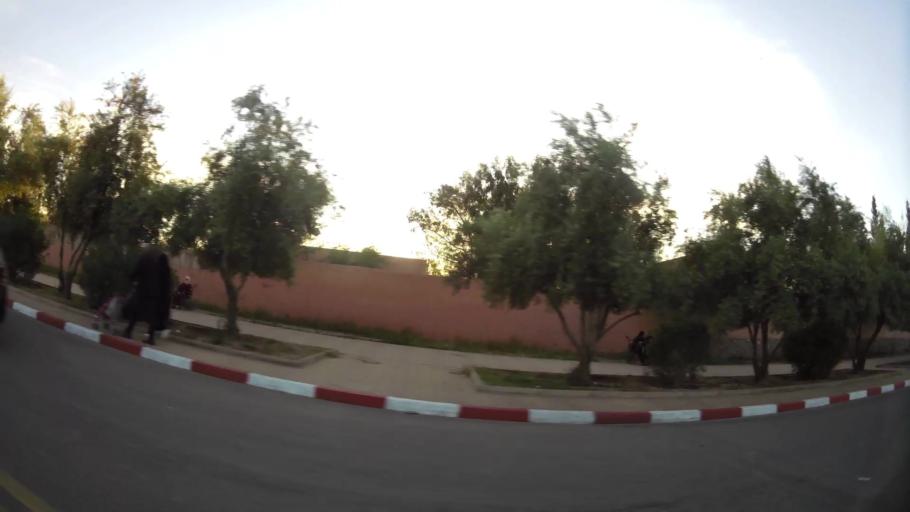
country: MA
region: Marrakech-Tensift-Al Haouz
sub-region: Marrakech
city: Marrakesh
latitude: 31.6393
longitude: -8.0313
